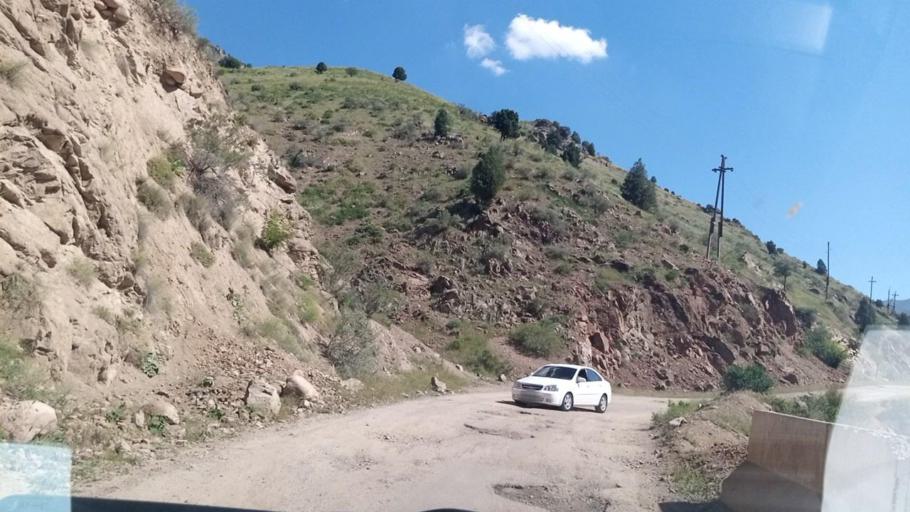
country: UZ
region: Toshkent
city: Yangiobod
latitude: 41.1294
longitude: 70.1109
